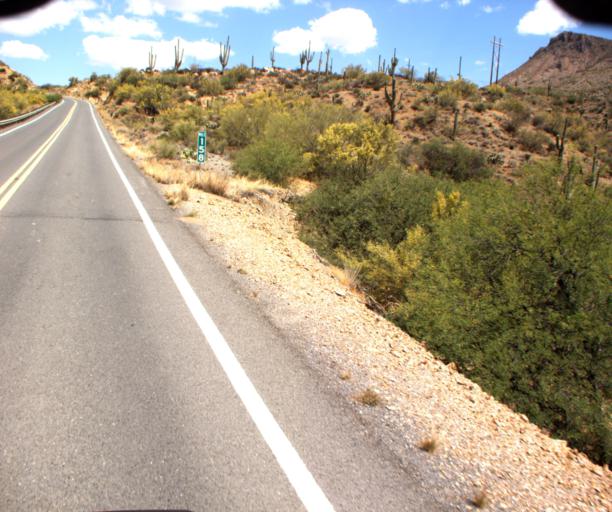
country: US
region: Arizona
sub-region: Pinal County
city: Superior
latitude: 33.1770
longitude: -111.0365
